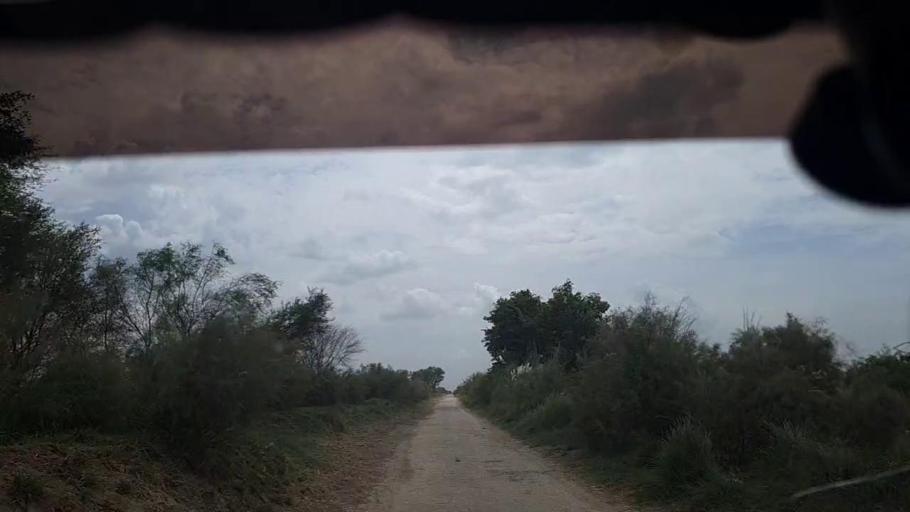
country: PK
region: Sindh
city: Rustam jo Goth
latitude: 28.0362
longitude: 68.9383
